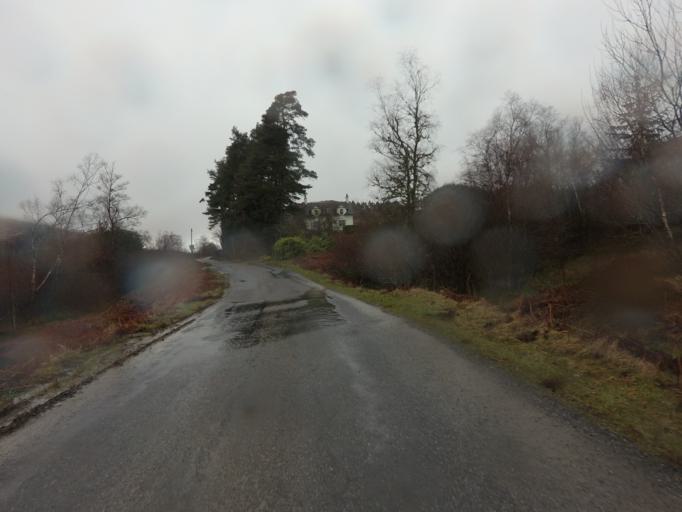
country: GB
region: Scotland
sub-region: West Dunbartonshire
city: Balloch
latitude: 56.2360
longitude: -4.5618
